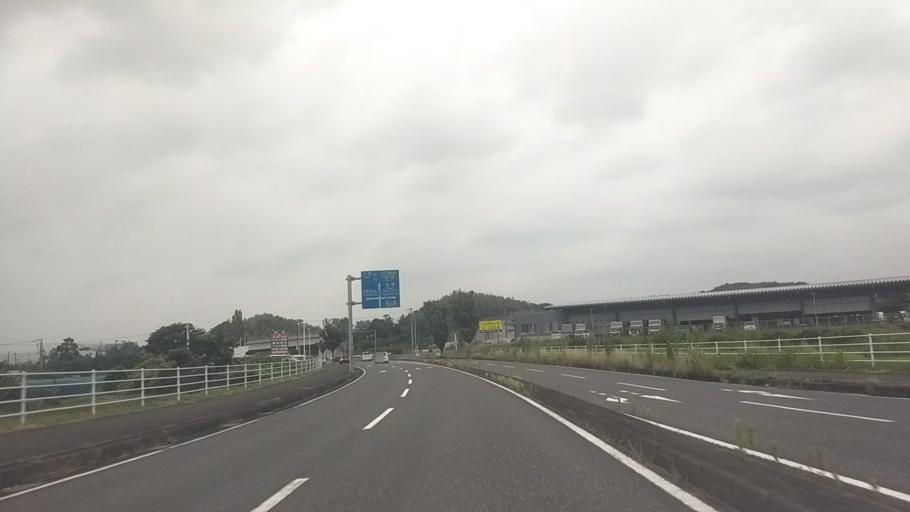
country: JP
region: Chiba
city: Kisarazu
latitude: 35.3862
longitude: 139.9699
